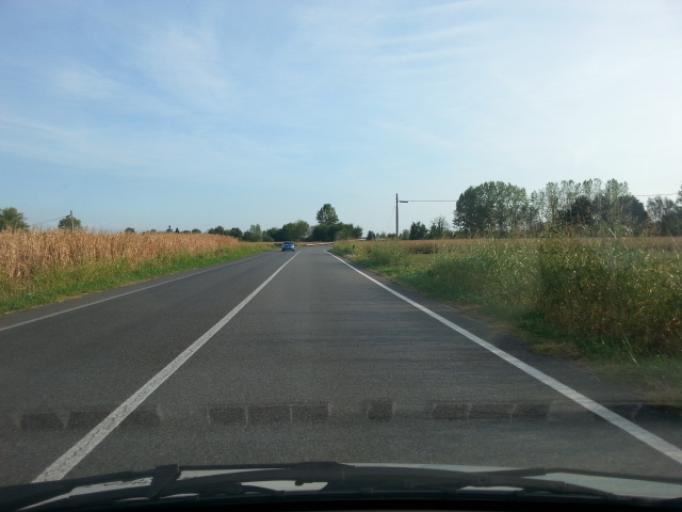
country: IT
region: Piedmont
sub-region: Provincia di Torino
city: Rivalta di Torino
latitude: 45.0259
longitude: 7.5315
